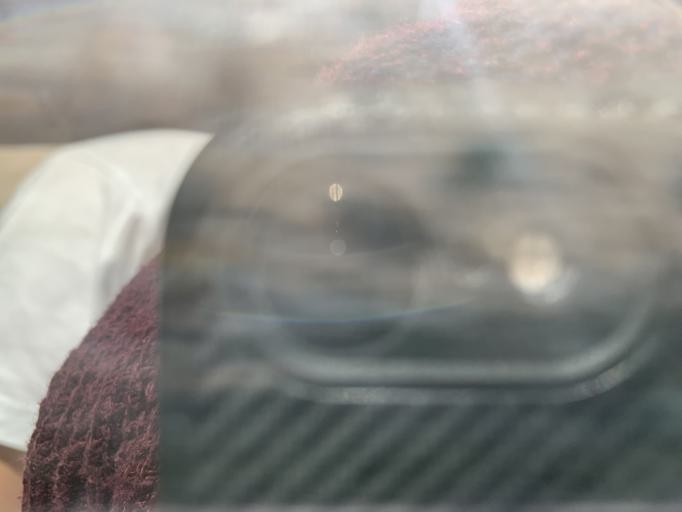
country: ES
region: Catalonia
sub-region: Provincia de Tarragona
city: Montblanc
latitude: 41.3589
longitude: 1.1907
